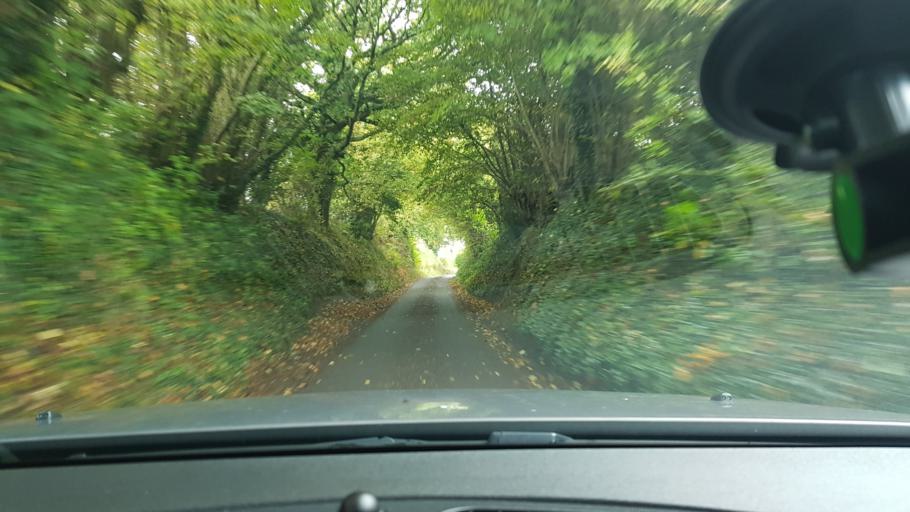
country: GB
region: England
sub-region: Wiltshire
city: Burbage
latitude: 51.3522
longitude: -1.7028
